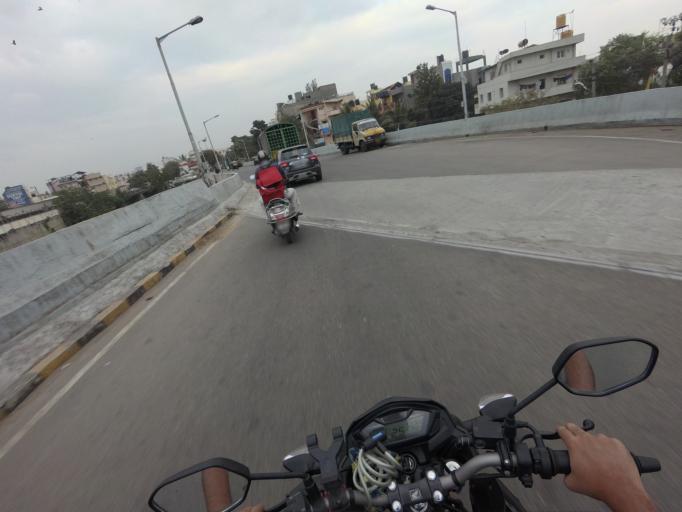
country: IN
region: Karnataka
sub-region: Bangalore Urban
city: Bangalore
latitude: 12.9663
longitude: 77.5455
